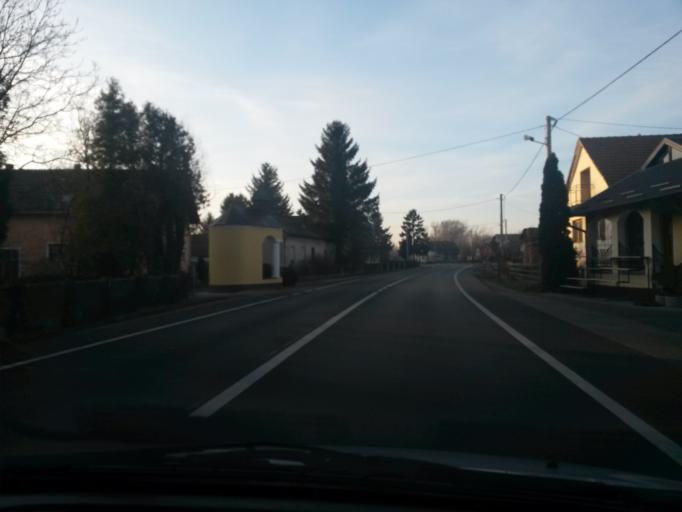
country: HR
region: Varazdinska
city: Jalzabet
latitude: 46.3028
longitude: 16.4727
